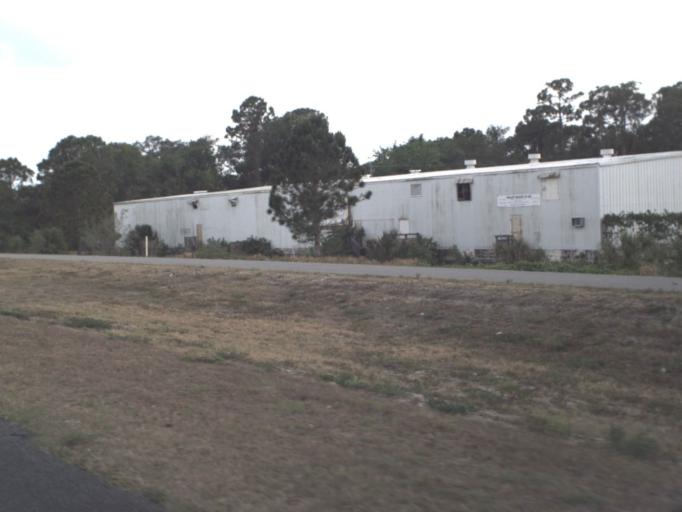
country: US
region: Florida
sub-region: Brevard County
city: Titusville
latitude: 28.6262
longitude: -80.8235
